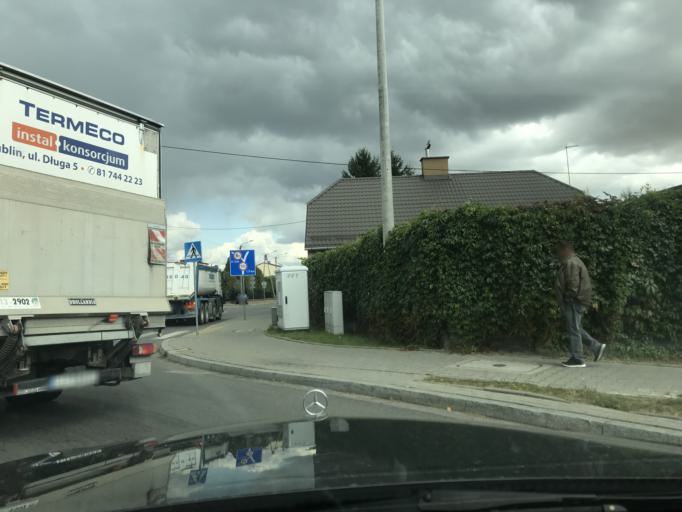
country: PL
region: Lublin Voivodeship
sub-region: Powiat lubartowski
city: Lubartow
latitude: 51.4720
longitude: 22.6064
